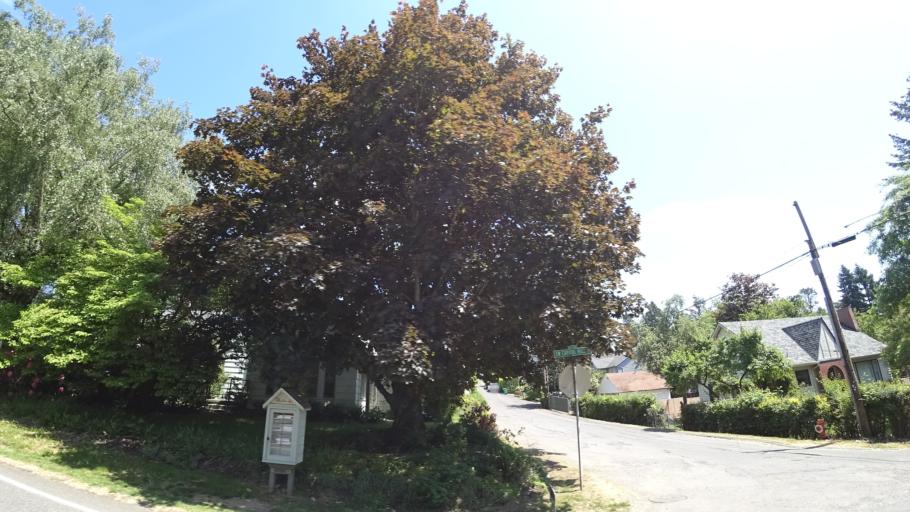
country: US
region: Oregon
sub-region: Clackamas County
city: Lake Oswego
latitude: 45.4690
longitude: -122.7000
